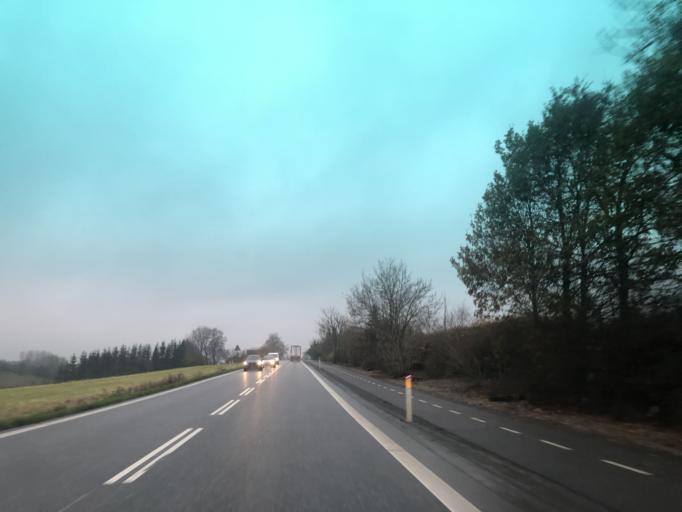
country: DK
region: South Denmark
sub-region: Nyborg Kommune
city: Ullerslev
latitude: 55.2697
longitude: 10.6765
